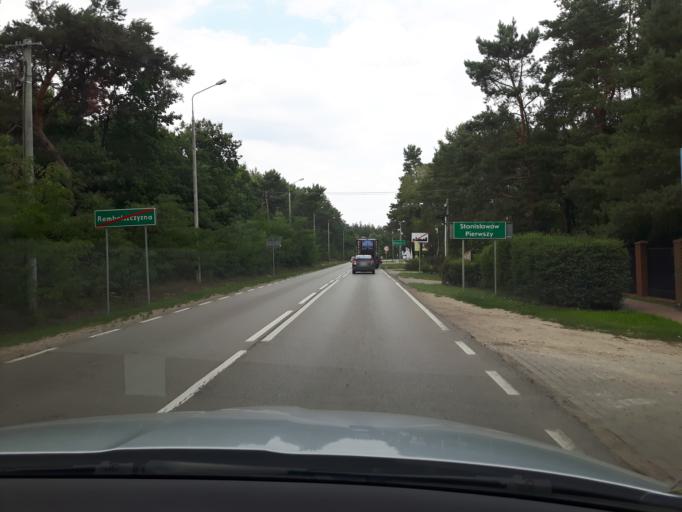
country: PL
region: Masovian Voivodeship
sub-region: Powiat legionowski
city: Stanislawow Pierwszy
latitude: 52.3814
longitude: 21.0292
